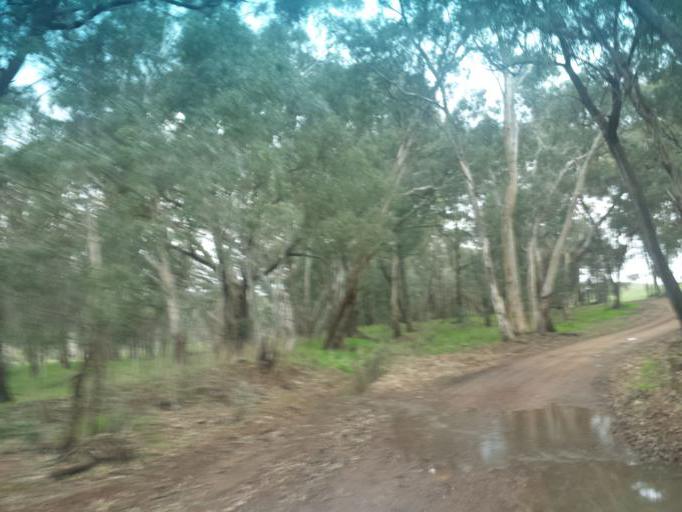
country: AU
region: Victoria
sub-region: Murrindindi
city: Kinglake West
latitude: -36.9894
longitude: 145.2219
